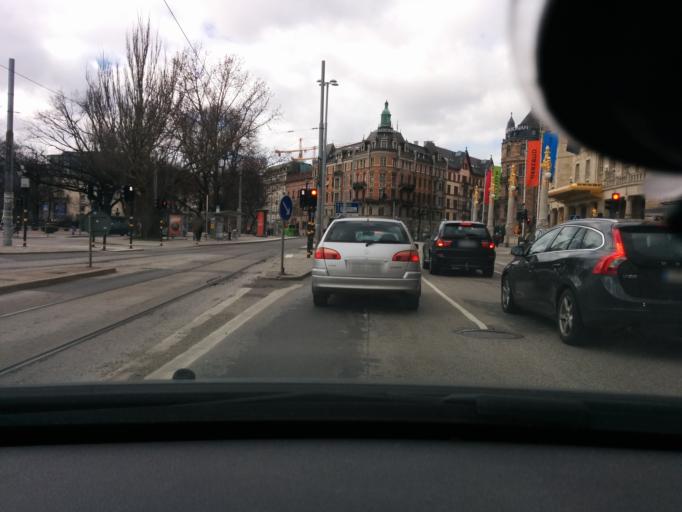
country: SE
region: Stockholm
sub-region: Stockholms Kommun
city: OEstermalm
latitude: 59.3325
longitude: 18.0779
